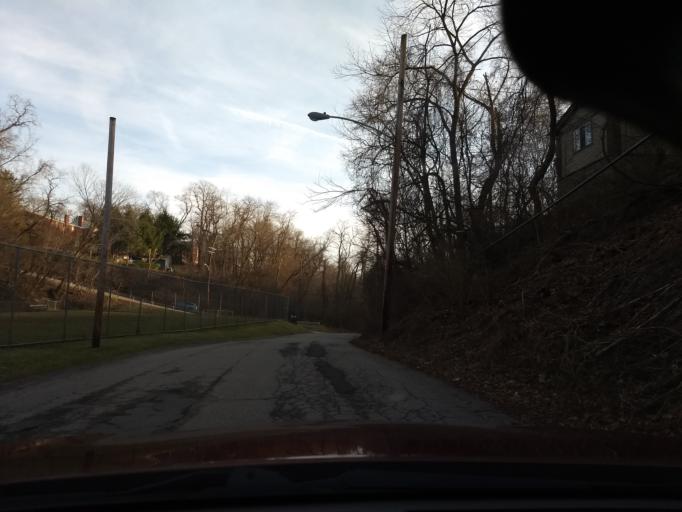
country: US
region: Pennsylvania
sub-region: Allegheny County
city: Brentwood
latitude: 40.3797
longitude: -79.9706
